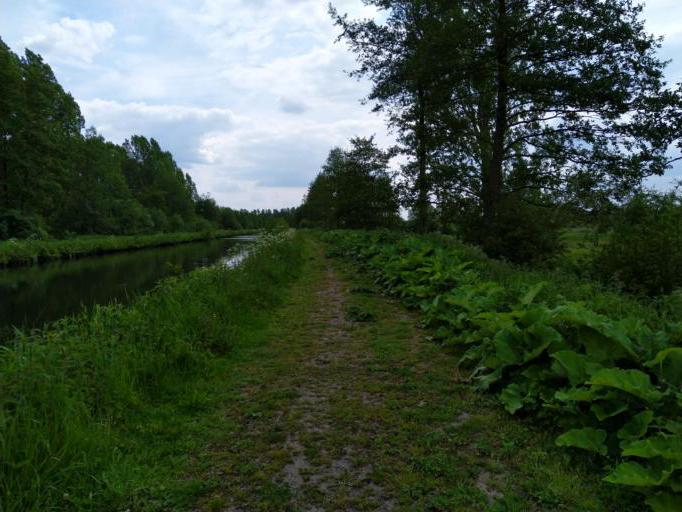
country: FR
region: Nord-Pas-de-Calais
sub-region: Departement du Nord
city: Bousies
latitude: 50.0973
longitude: 3.6333
